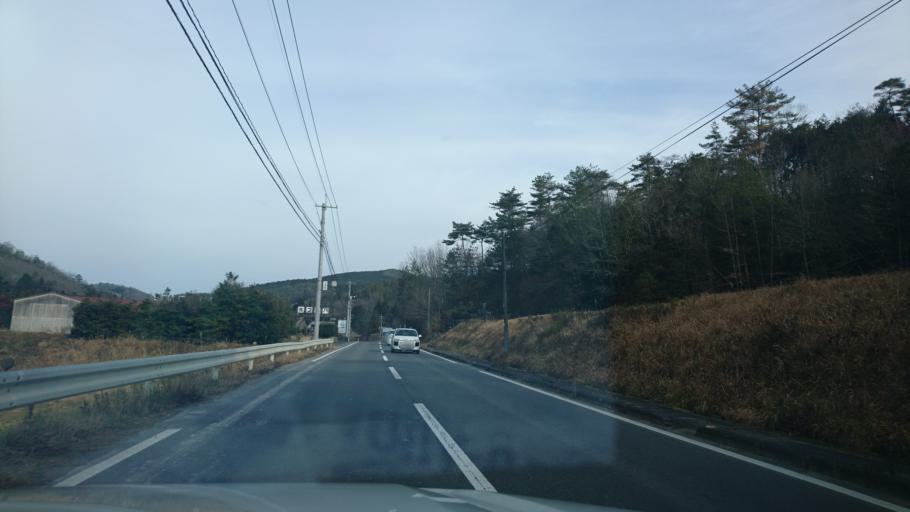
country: JP
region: Okayama
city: Takahashi
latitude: 34.8123
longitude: 133.6738
